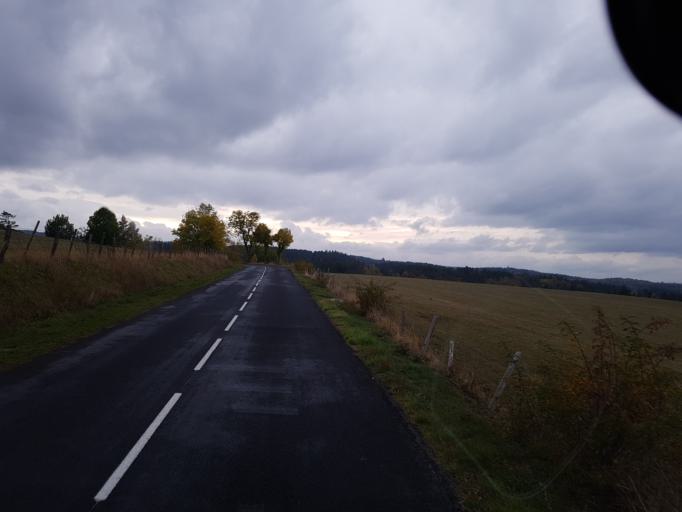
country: FR
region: Languedoc-Roussillon
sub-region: Departement de la Lozere
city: Langogne
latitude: 44.7202
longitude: 3.8174
